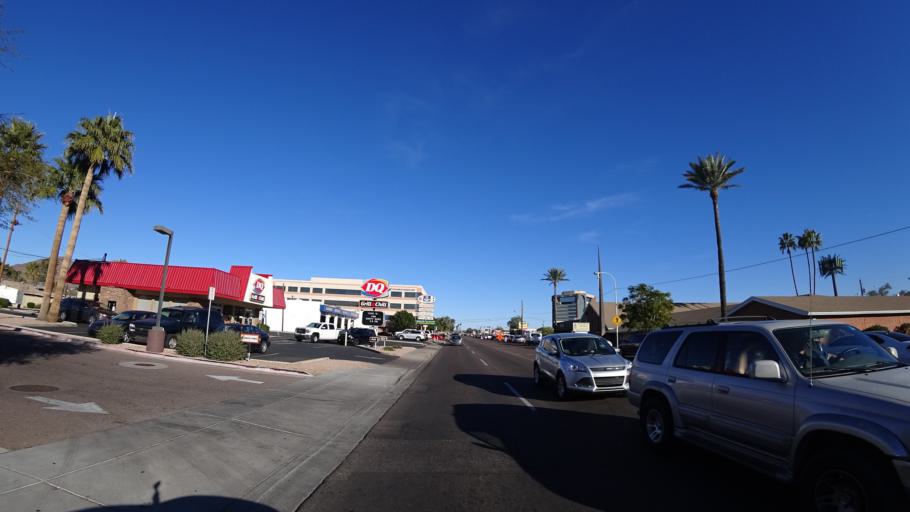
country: US
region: Arizona
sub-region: Maricopa County
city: Paradise Valley
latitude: 33.4805
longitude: -111.9923
